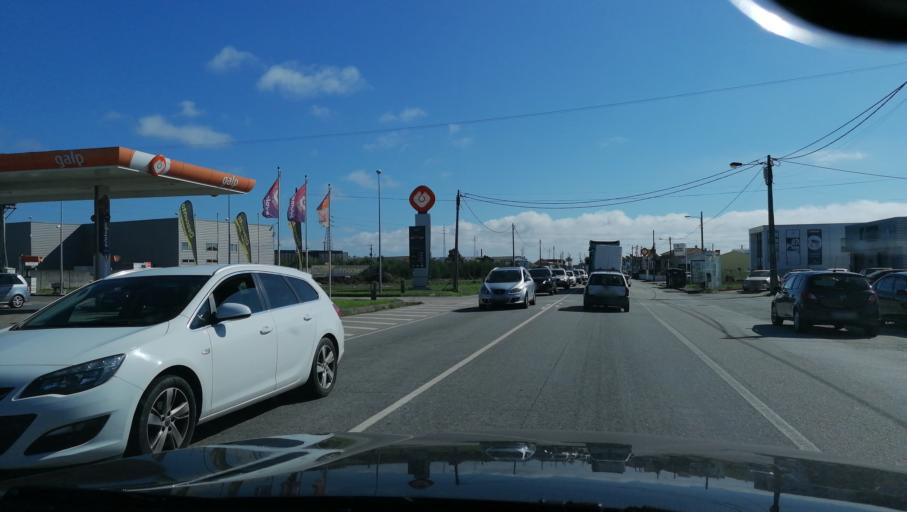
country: PT
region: Aveiro
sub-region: Aveiro
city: Aveiro
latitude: 40.6663
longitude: -8.6096
